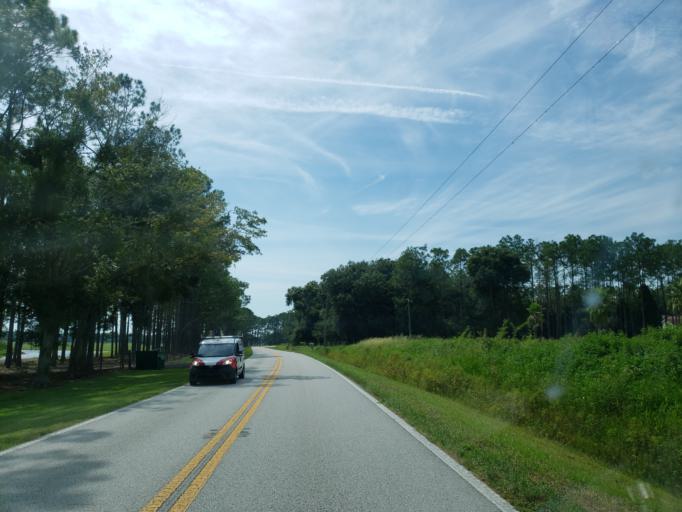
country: US
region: Florida
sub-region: Pasco County
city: San Antonio
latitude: 28.3910
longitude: -82.3068
